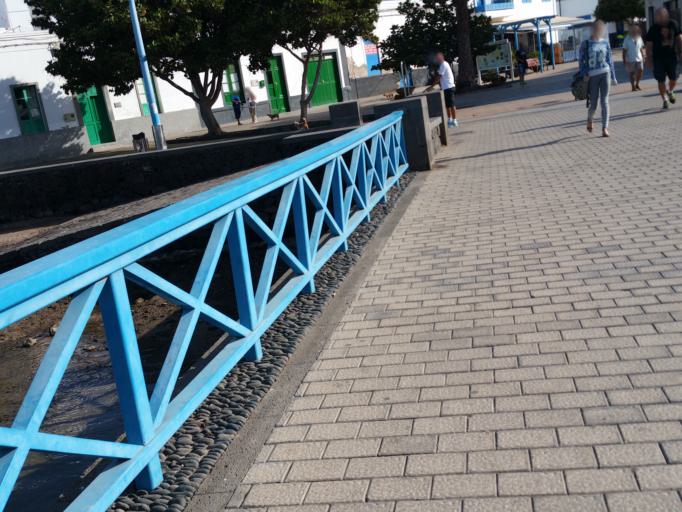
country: ES
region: Canary Islands
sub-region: Provincia de Las Palmas
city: Arrecife
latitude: 28.9613
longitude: -13.5444
